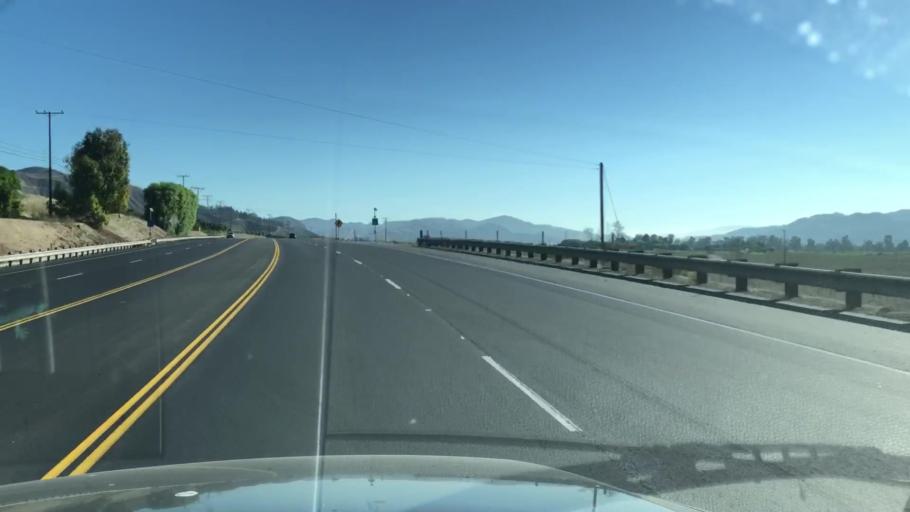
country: US
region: California
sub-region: Ventura County
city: Piru
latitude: 34.3984
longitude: -118.8436
